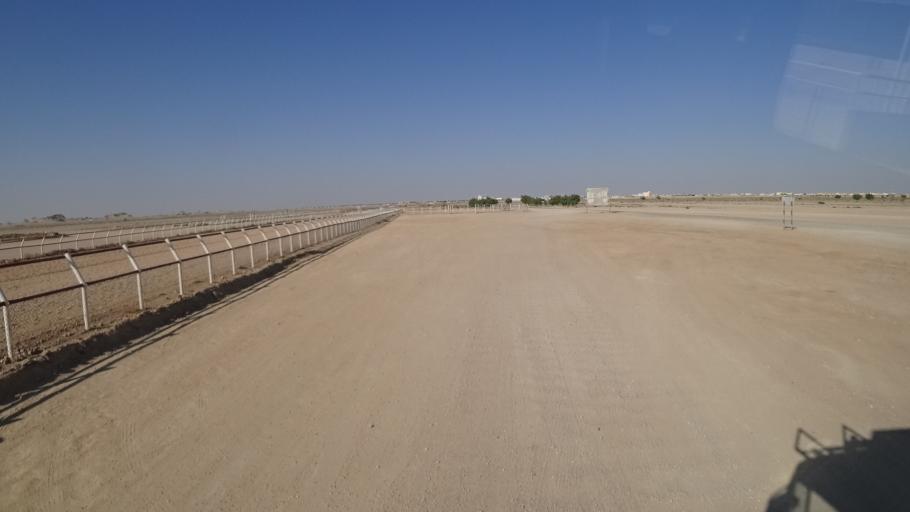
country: OM
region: Zufar
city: Salalah
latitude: 17.5937
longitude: 54.0256
